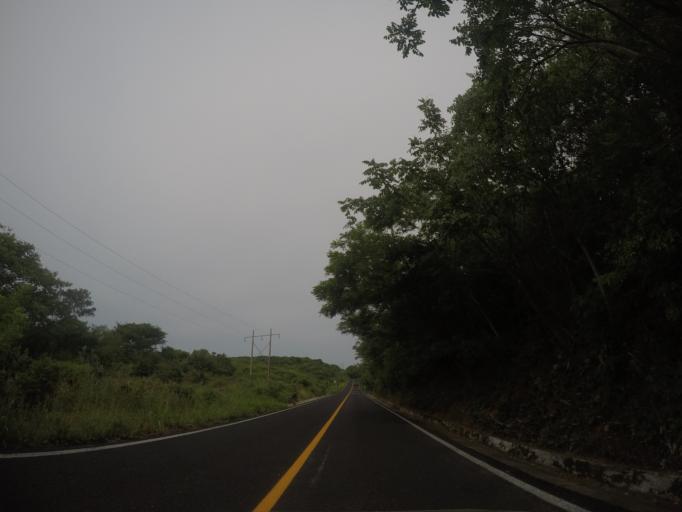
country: MX
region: Oaxaca
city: San Pedro Mixtepec
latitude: 15.9489
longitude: -97.2897
